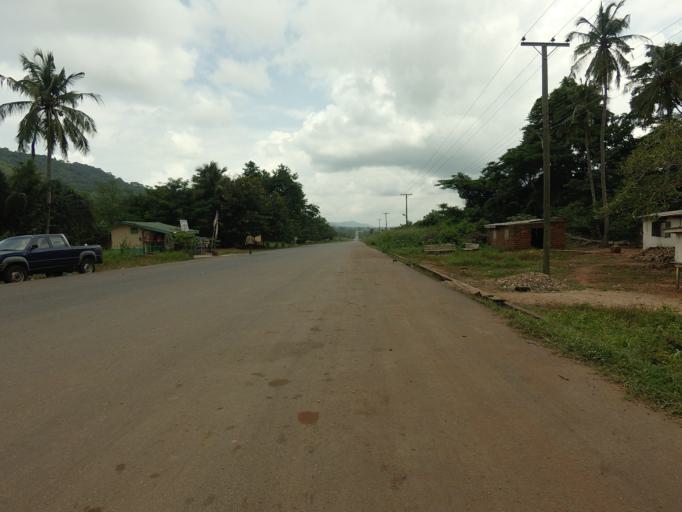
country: GH
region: Volta
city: Ho
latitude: 6.6224
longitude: 0.3083
